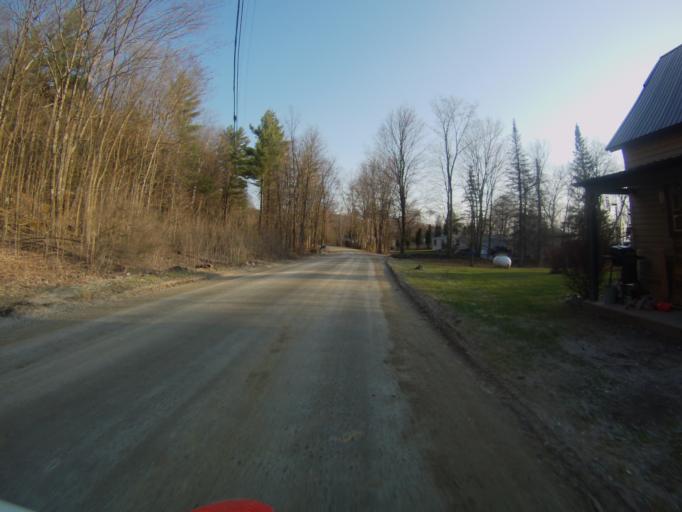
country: US
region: Vermont
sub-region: Addison County
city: Bristol
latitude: 44.1104
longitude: -73.0767
